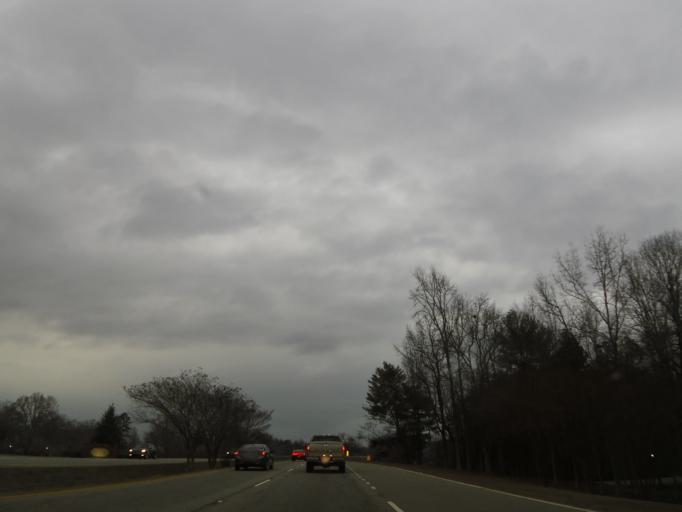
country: US
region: South Carolina
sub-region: Greenville County
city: Berea
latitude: 34.9237
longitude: -82.4330
